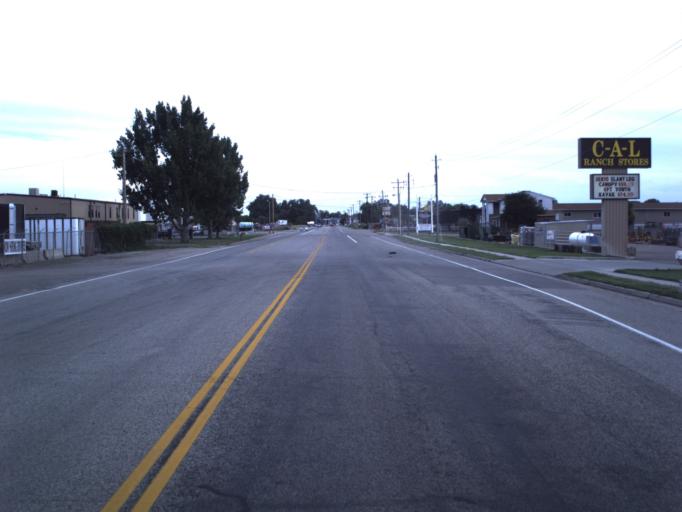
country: US
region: Utah
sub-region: Weber County
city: Farr West
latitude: 41.2755
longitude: -112.0282
